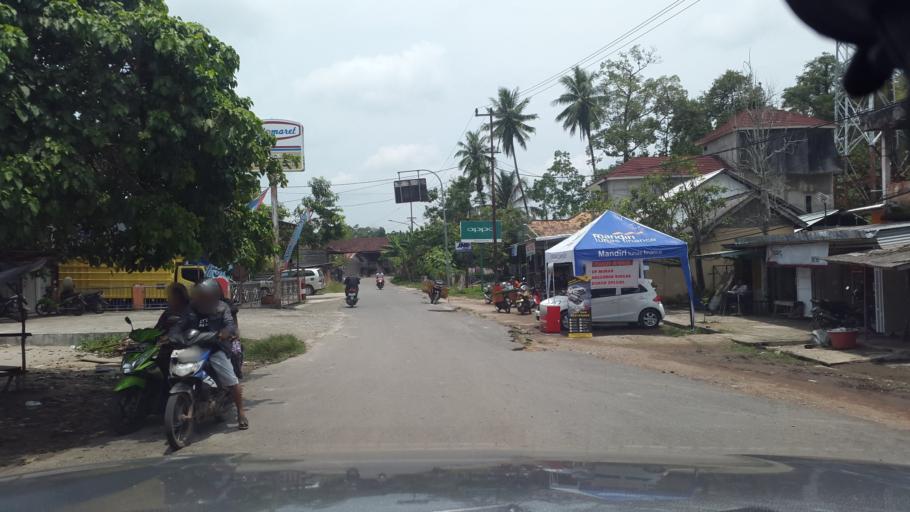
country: ID
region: South Sumatra
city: Tanjung Lubuk
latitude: -3.2691
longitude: 104.8762
